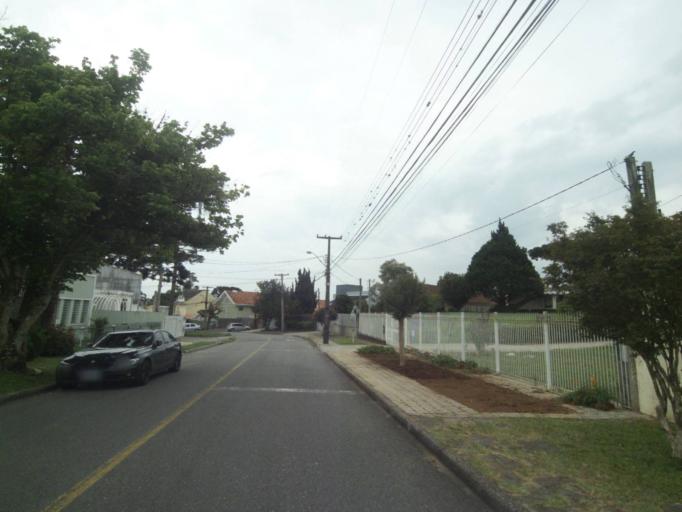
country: BR
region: Parana
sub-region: Curitiba
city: Curitiba
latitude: -25.4105
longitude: -49.2978
